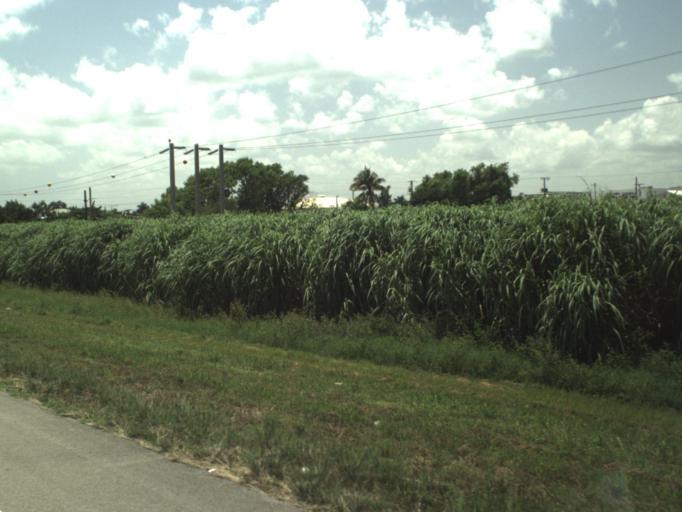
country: US
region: Florida
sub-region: Palm Beach County
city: Belle Glade
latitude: 26.6997
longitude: -80.6681
